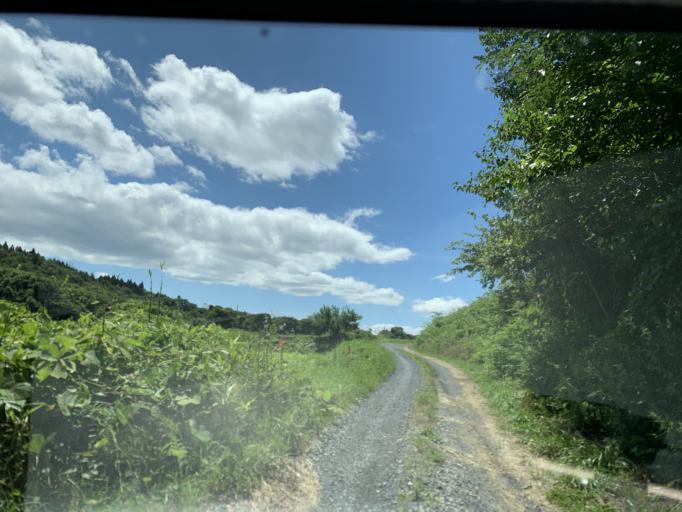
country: JP
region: Iwate
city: Ichinoseki
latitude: 38.9233
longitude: 141.0717
